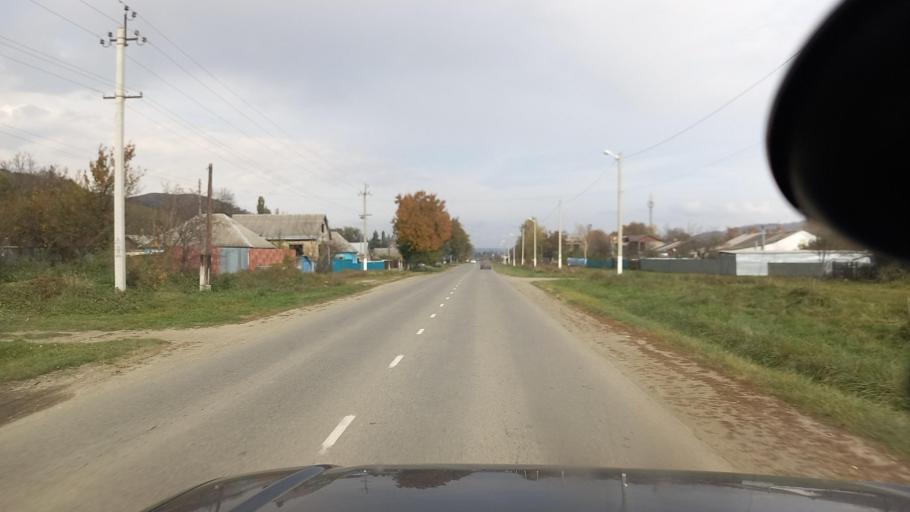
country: RU
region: Krasnodarskiy
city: Psebay
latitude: 44.1370
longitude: 40.8175
